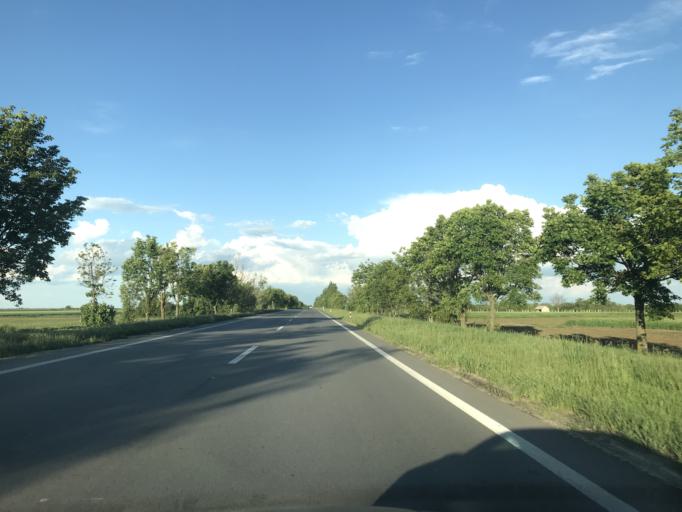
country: RS
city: Aradac
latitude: 45.3908
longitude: 20.2759
